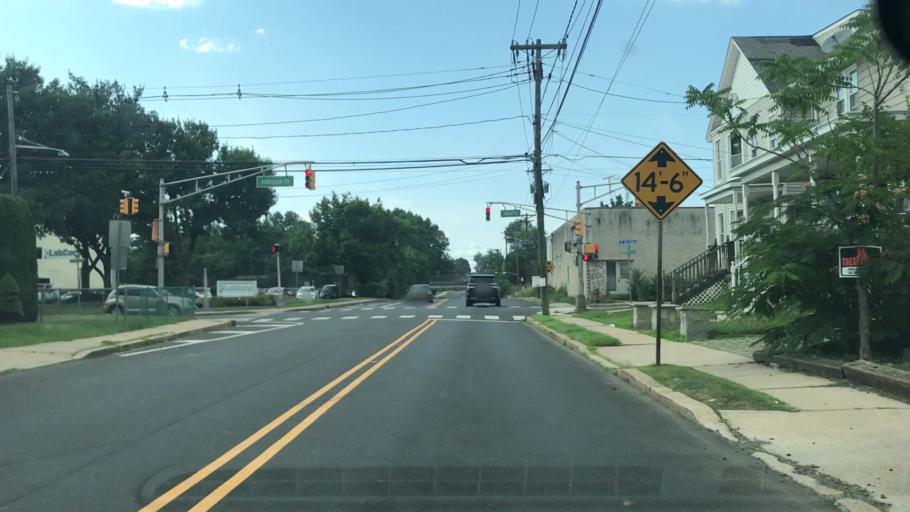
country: US
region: New Jersey
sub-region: Somerset County
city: Raritan
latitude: 40.5692
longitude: -74.6380
